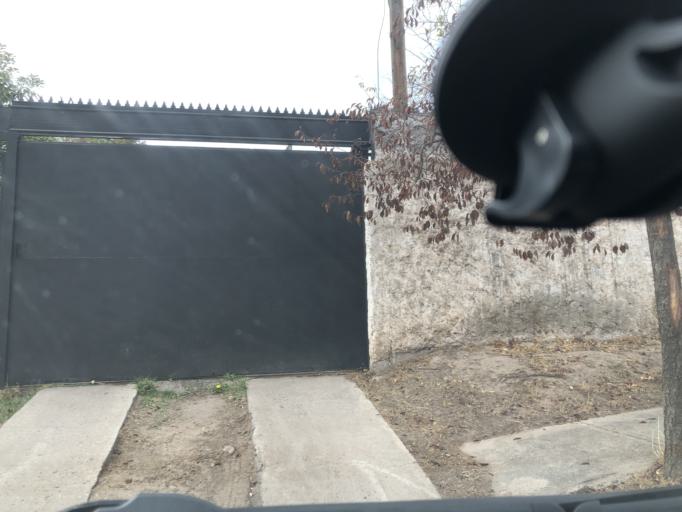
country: CL
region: Santiago Metropolitan
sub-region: Provincia de Cordillera
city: Puente Alto
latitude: -33.6129
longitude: -70.5331
